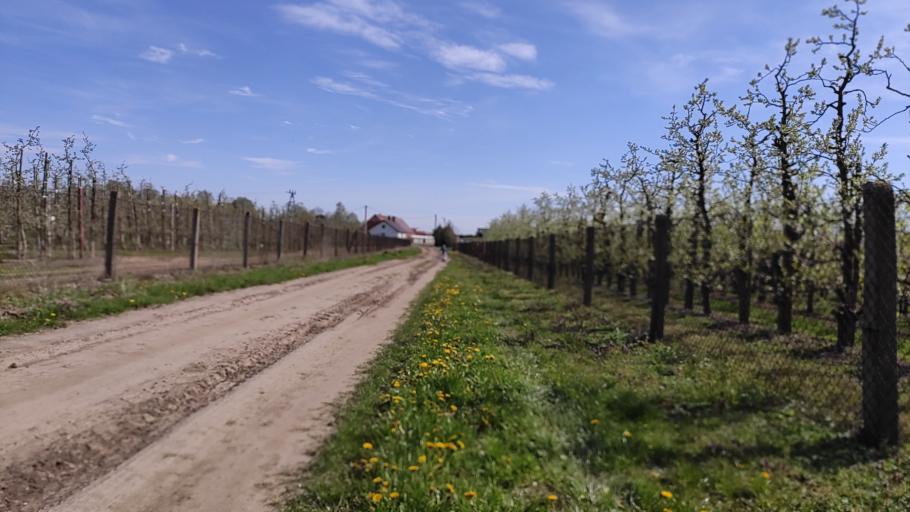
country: PL
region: Greater Poland Voivodeship
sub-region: Powiat poznanski
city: Kostrzyn
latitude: 52.3997
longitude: 17.1771
